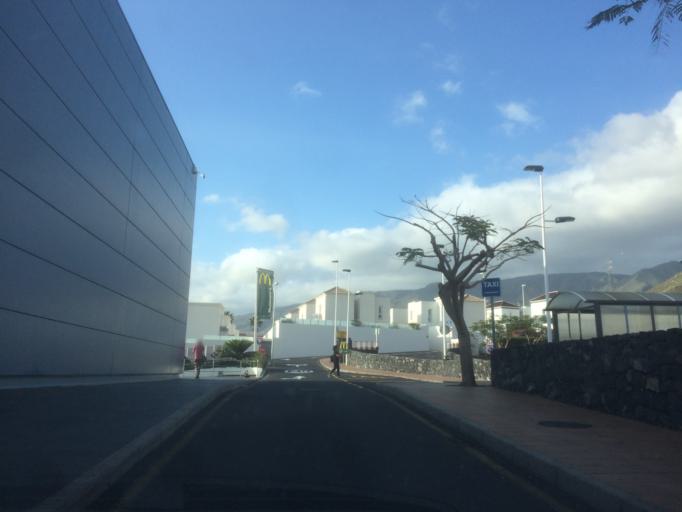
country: ES
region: Canary Islands
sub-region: Provincia de Santa Cruz de Tenerife
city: Playa de las Americas
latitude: 28.0883
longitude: -16.7279
